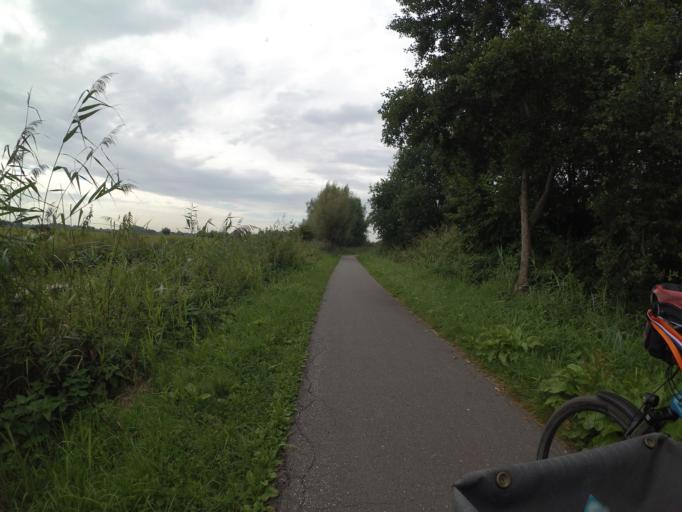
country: NL
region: North Brabant
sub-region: Roosendaal
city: Roosendaal
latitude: 51.5038
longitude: 4.4525
